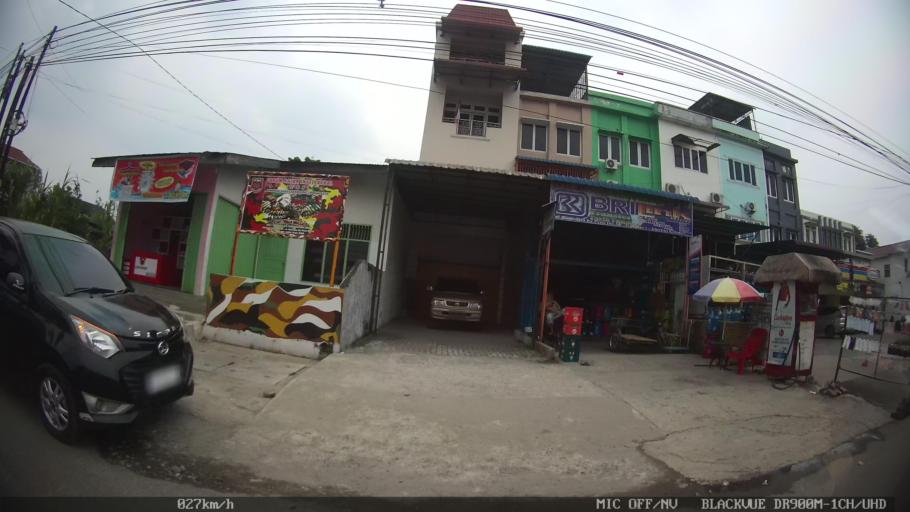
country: ID
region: North Sumatra
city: Medan
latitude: 3.5613
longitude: 98.7030
